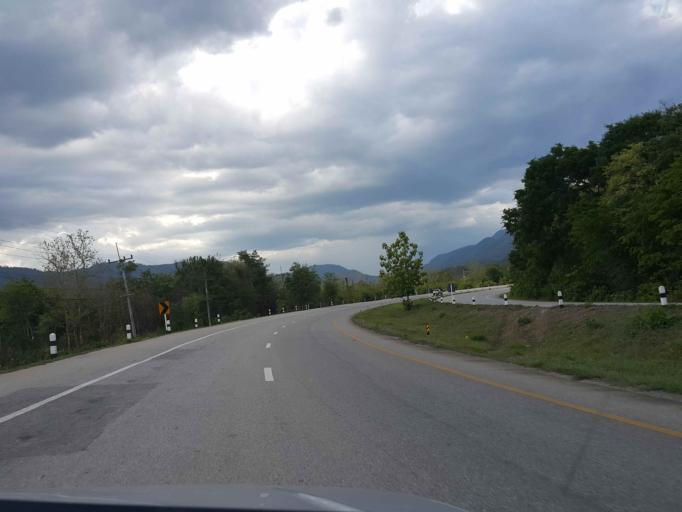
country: TH
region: Lampang
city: Thoen
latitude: 17.7427
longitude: 99.2309
